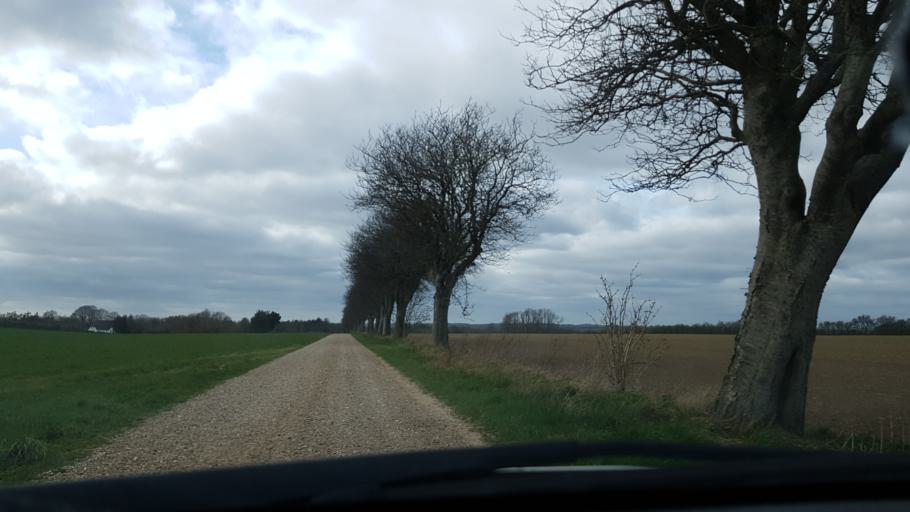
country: DK
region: South Denmark
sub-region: Vejen Kommune
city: Brorup
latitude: 55.4248
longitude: 9.0255
